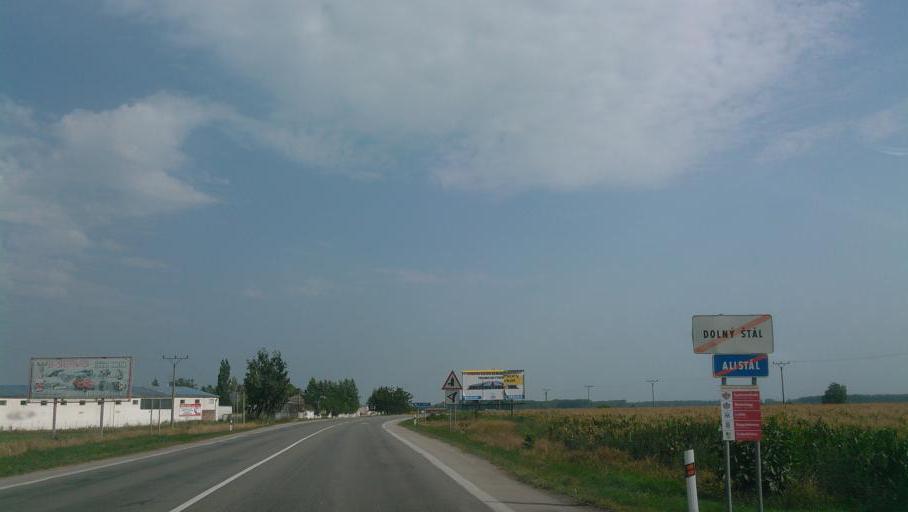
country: SK
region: Trnavsky
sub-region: Okres Dunajska Streda
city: Velky Meder
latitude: 47.9352
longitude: 17.7213
